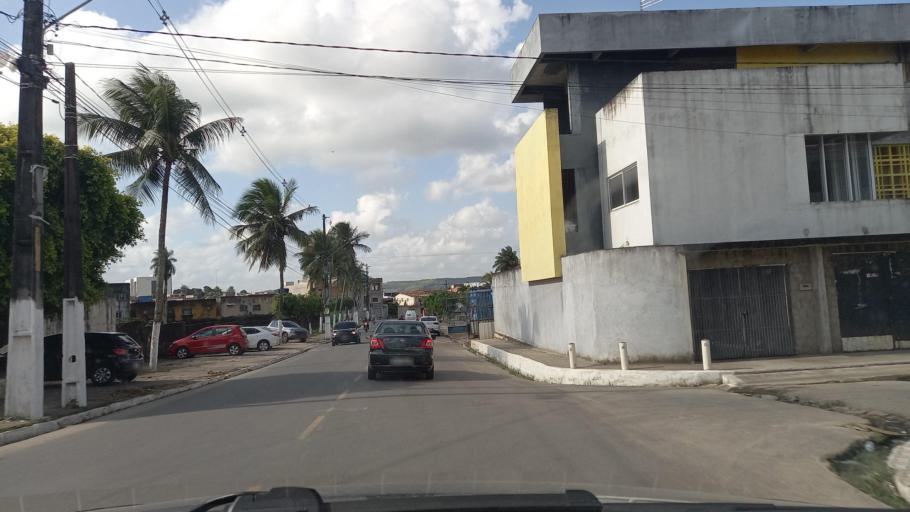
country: BR
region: Pernambuco
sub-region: Goiana
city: Goiana
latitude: -7.5609
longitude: -35.0121
